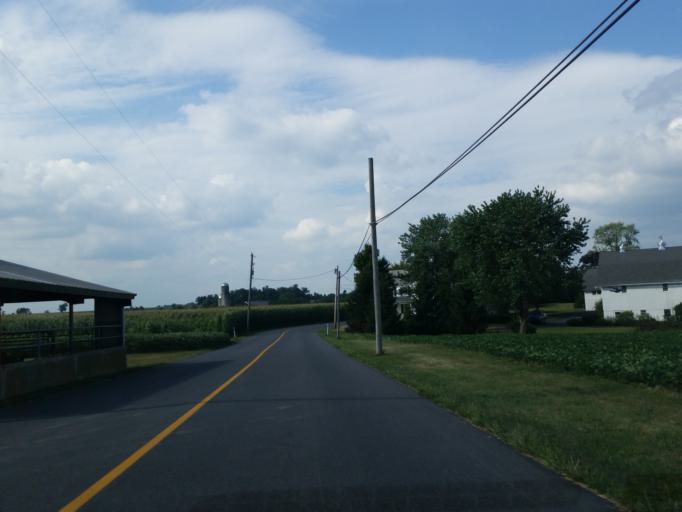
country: US
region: Pennsylvania
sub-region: Lancaster County
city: Mount Joy
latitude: 40.1468
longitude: -76.4646
